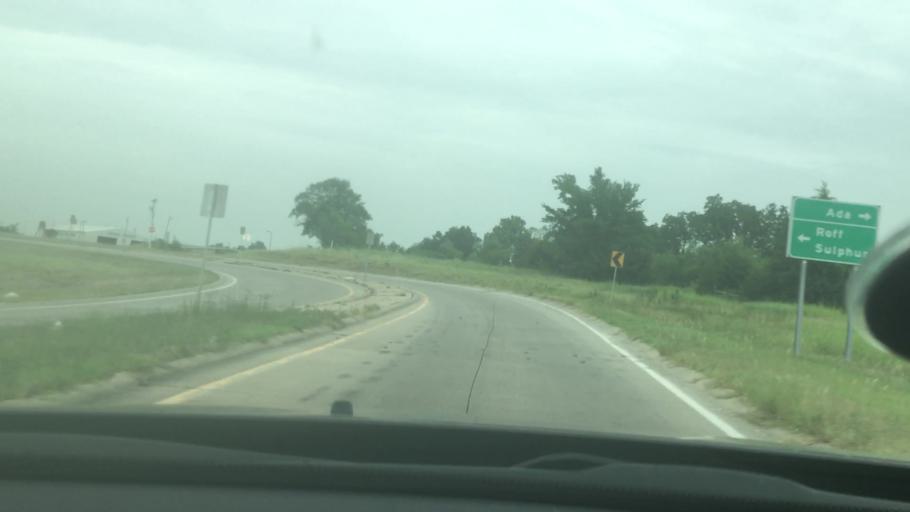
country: US
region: Oklahoma
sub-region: Pontotoc County
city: Ada
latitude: 34.7637
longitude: -96.7001
